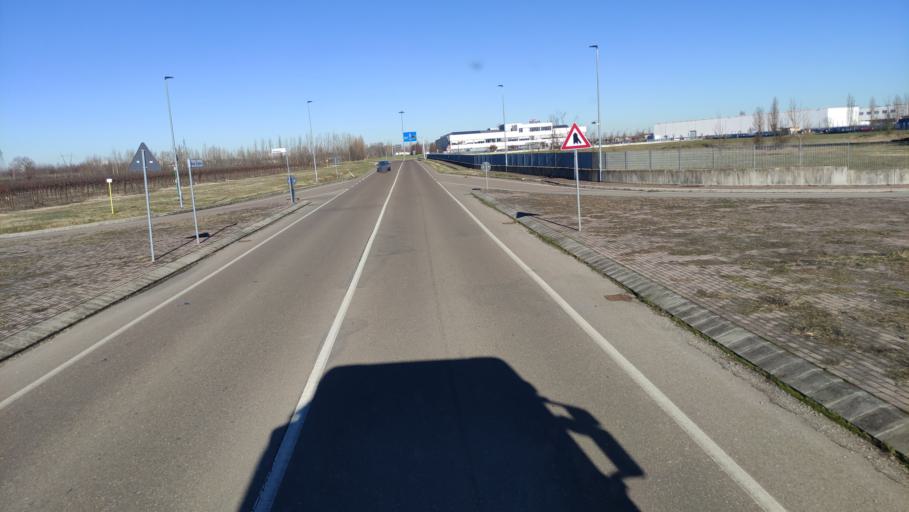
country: IT
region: Emilia-Romagna
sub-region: Provincia di Reggio Emilia
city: Correggio
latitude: 44.7694
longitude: 10.8121
